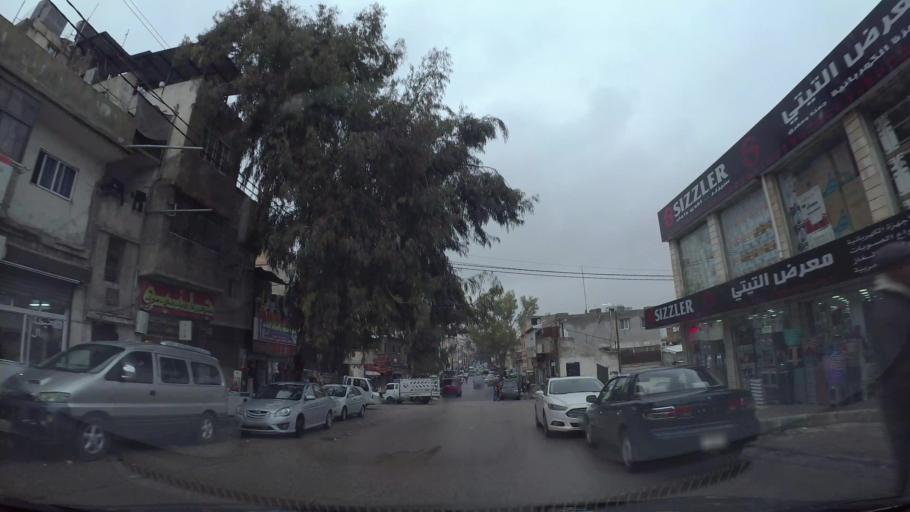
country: JO
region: Amman
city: Amman
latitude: 31.9621
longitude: 35.9276
